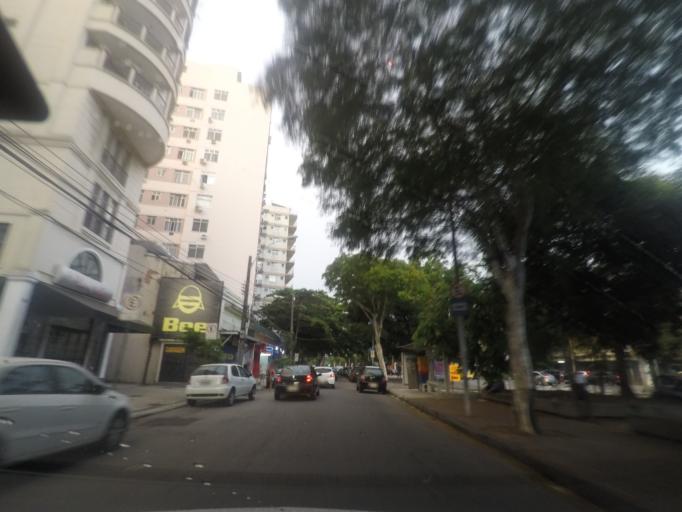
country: BR
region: Rio de Janeiro
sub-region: Rio De Janeiro
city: Rio de Janeiro
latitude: -22.9526
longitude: -43.1766
